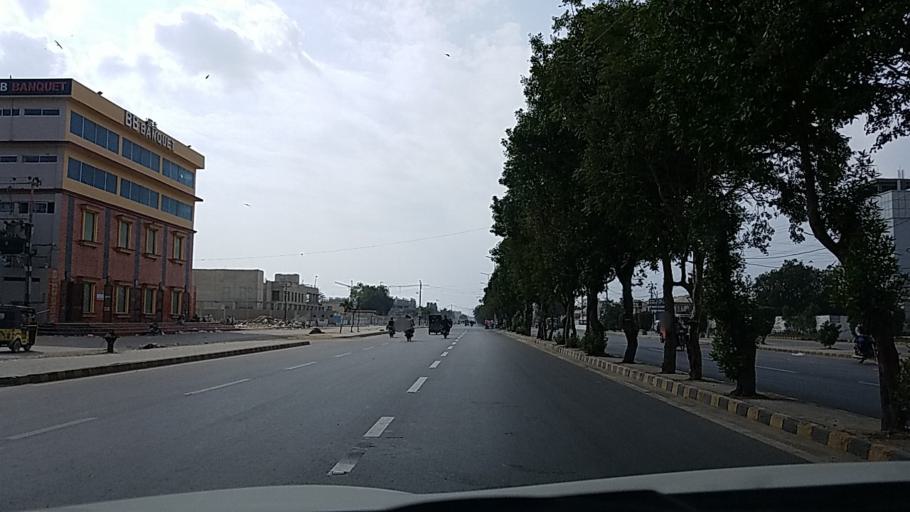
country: PK
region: Sindh
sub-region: Karachi District
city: Karachi
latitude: 24.8193
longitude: 67.1196
